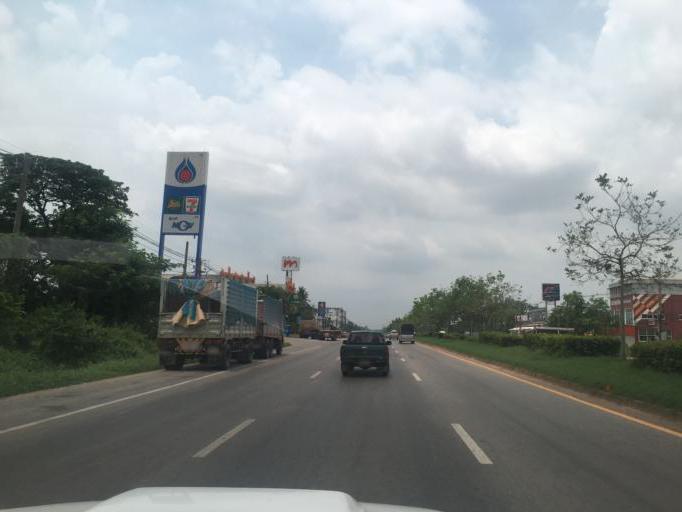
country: TH
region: Changwat Udon Thani
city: Udon Thani
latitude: 17.4039
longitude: 102.7661
